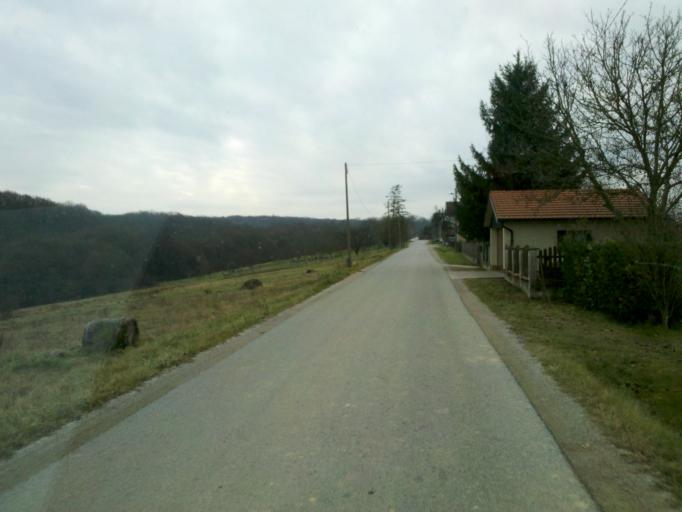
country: HR
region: Grad Zagreb
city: Horvati
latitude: 45.6656
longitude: 15.8218
